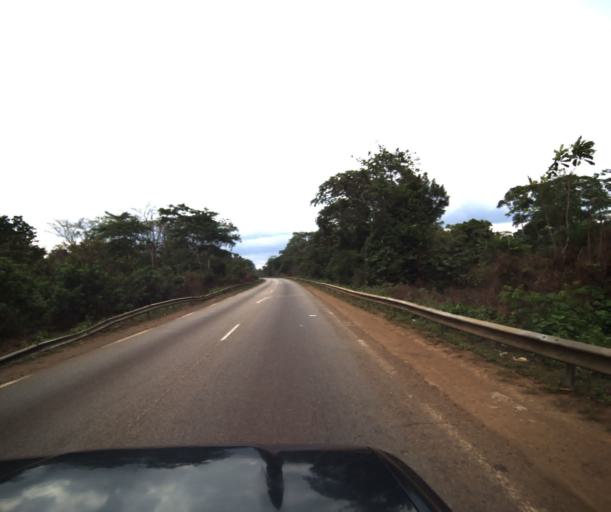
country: CM
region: Littoral
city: Edea
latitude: 3.9436
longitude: 10.0451
